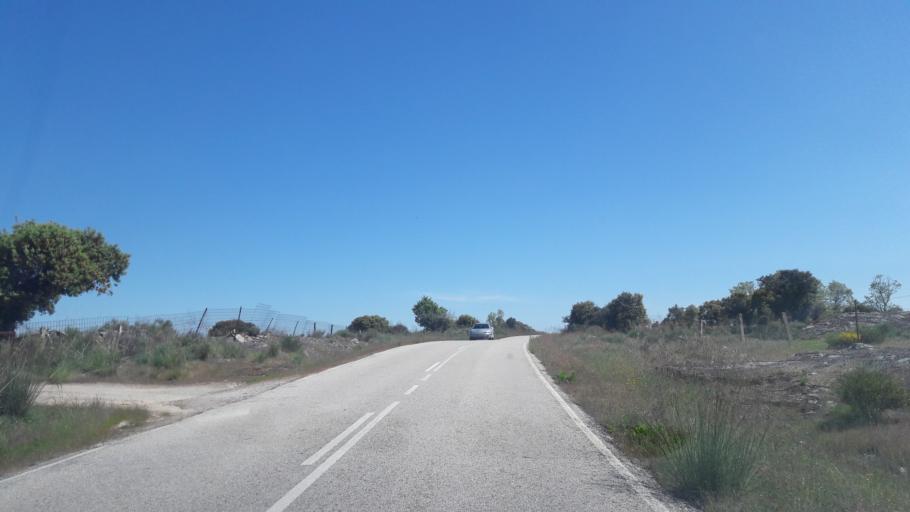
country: ES
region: Castille and Leon
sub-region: Provincia de Salamanca
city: Villarmuerto
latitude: 41.0416
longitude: -6.3912
